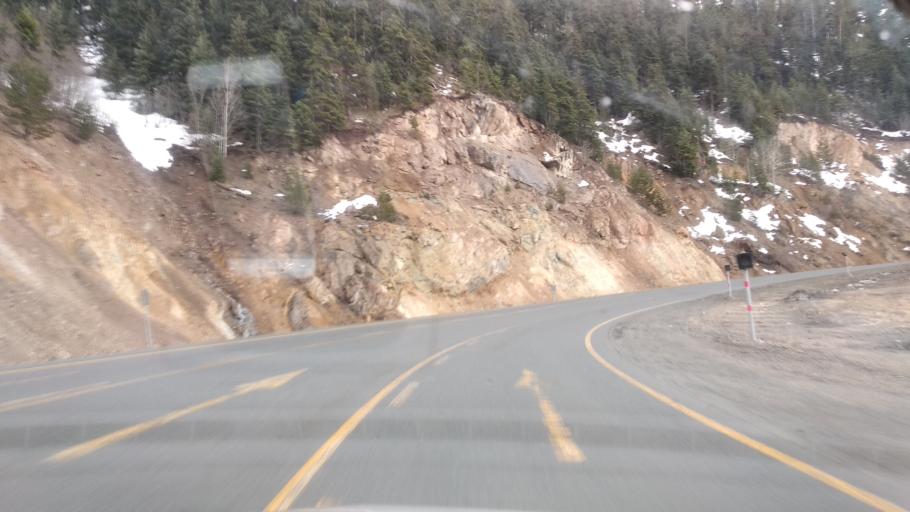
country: TR
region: Gumushane
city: Torul
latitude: 40.6486
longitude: 39.3610
